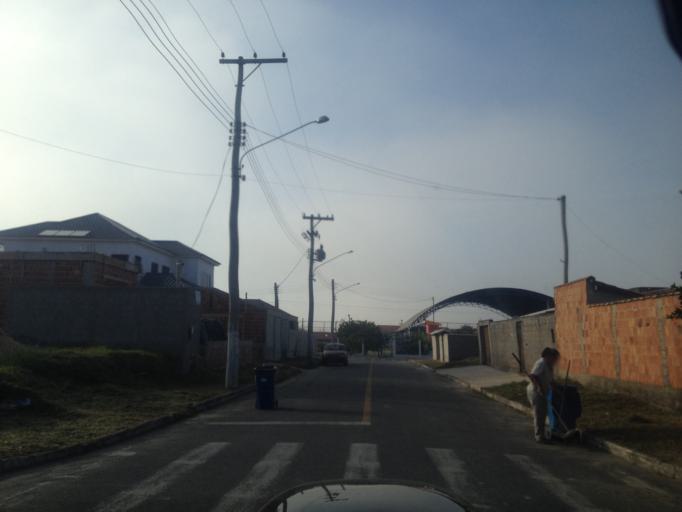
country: BR
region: Rio de Janeiro
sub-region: Porto Real
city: Porto Real
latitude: -22.4114
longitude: -44.3110
